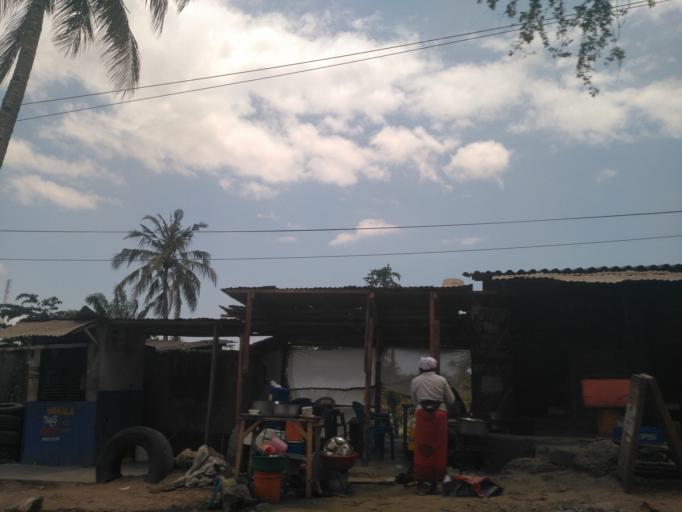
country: TZ
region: Dar es Salaam
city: Dar es Salaam
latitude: -6.8555
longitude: 39.2901
